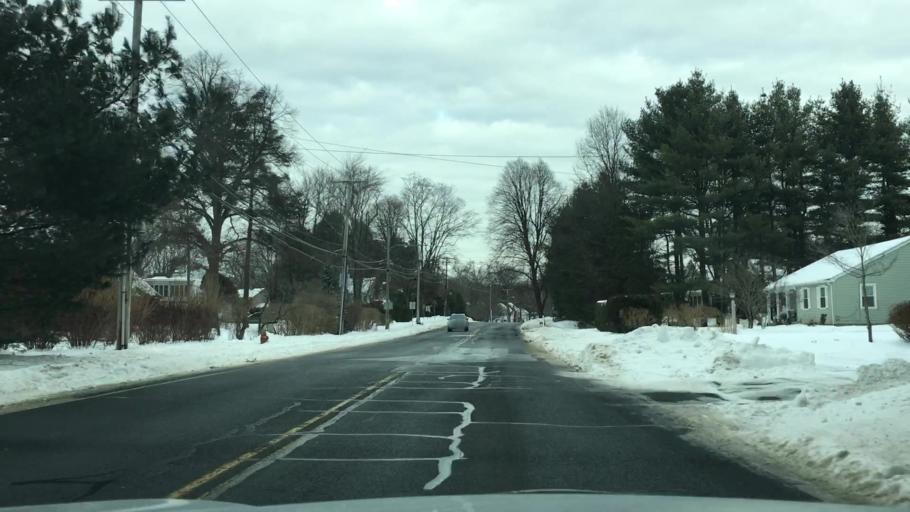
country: US
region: Massachusetts
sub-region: Hampden County
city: Longmeadow
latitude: 42.0473
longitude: -72.5732
